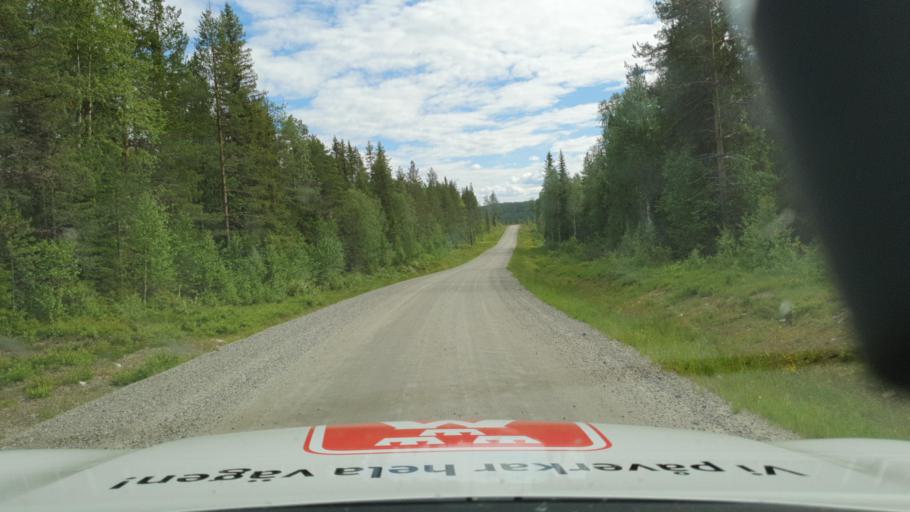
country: SE
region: Vaesterbotten
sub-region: Norsjo Kommun
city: Norsjoe
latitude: 64.8453
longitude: 19.5230
